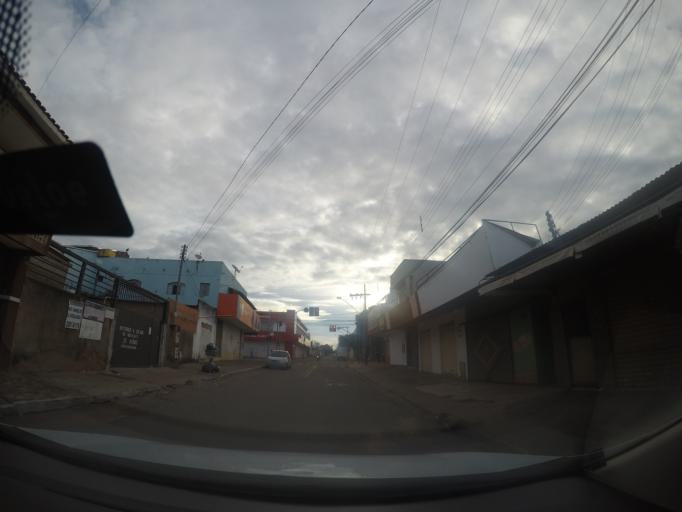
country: BR
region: Goias
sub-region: Goiania
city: Goiania
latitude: -16.6446
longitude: -49.3247
